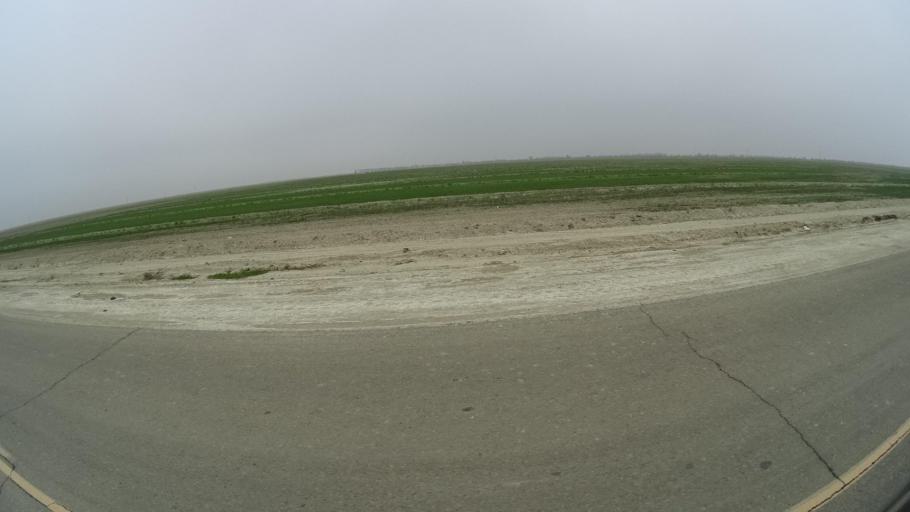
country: US
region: California
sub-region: Kern County
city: Rosedale
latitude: 35.2339
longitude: -119.2528
